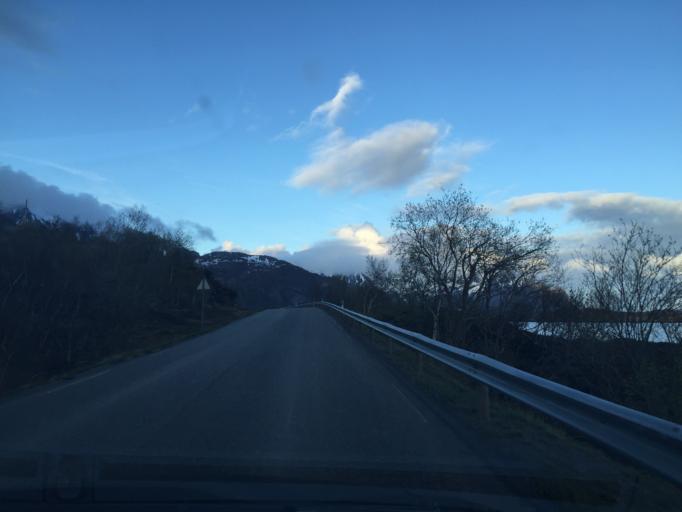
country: NO
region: Nordland
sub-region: Vagan
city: Svolvaer
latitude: 68.2840
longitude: 14.6646
